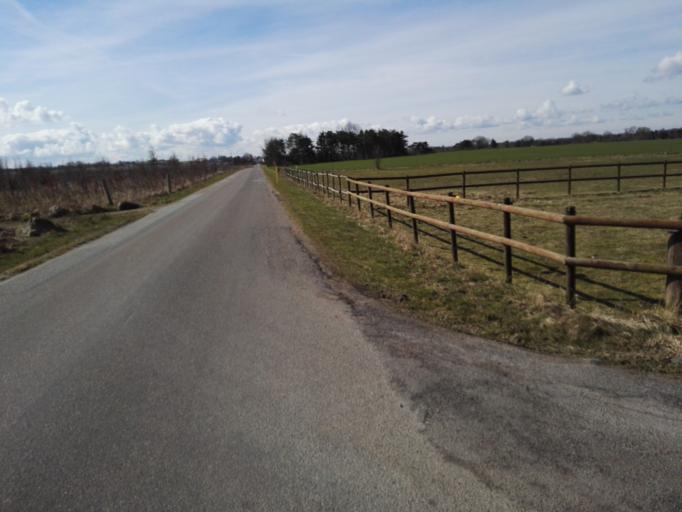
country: DK
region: Zealand
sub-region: Lejre Kommune
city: Ejby
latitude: 55.7801
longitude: 11.8297
